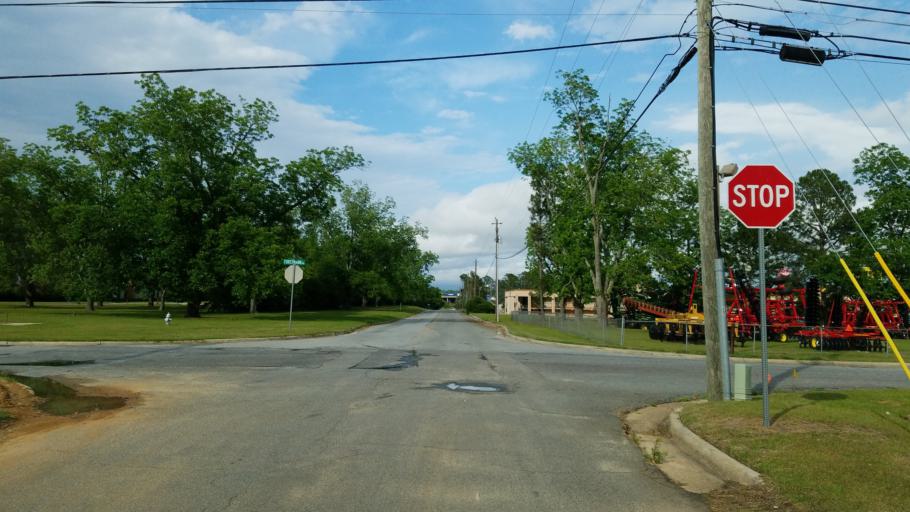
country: US
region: Georgia
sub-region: Tift County
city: Tifton
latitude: 31.4488
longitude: -83.5390
